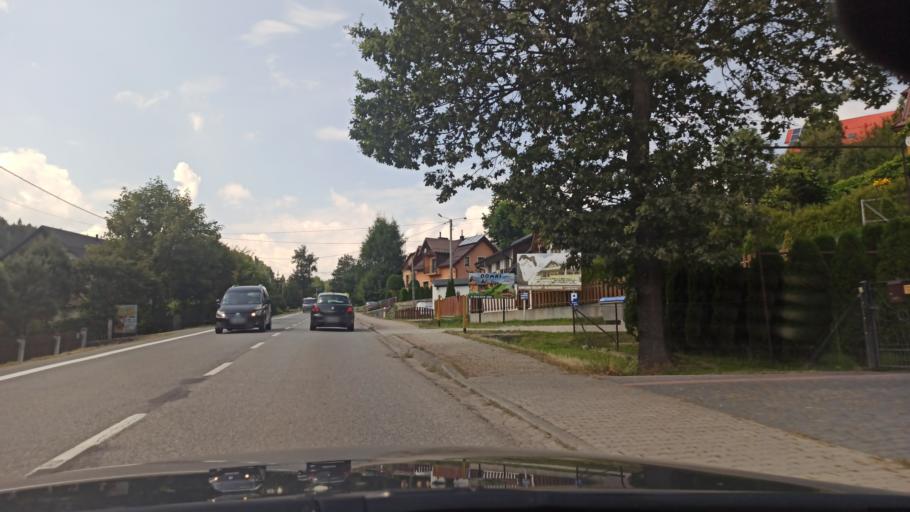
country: PL
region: Lesser Poland Voivodeship
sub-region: Powiat nowotarski
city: Krosnica
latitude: 49.4453
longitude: 20.3447
